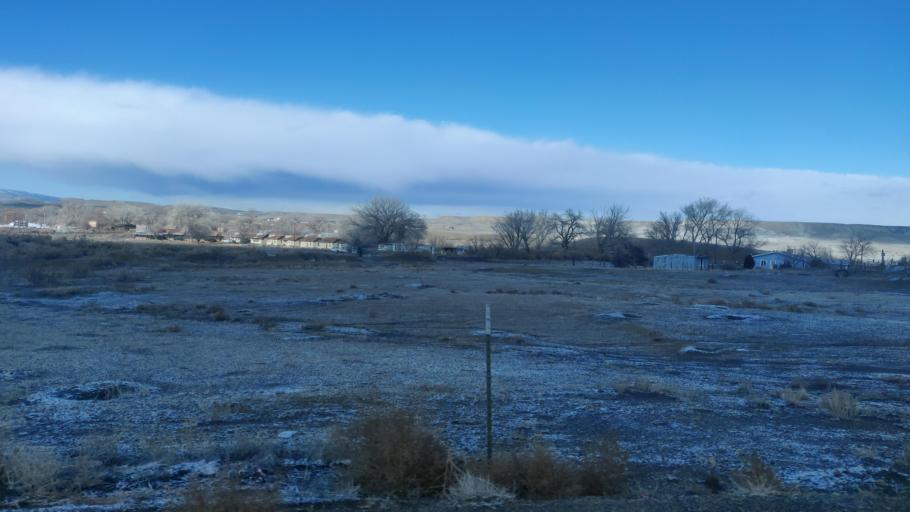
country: US
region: Colorado
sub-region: Mesa County
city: Clifton
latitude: 38.9880
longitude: -108.4448
